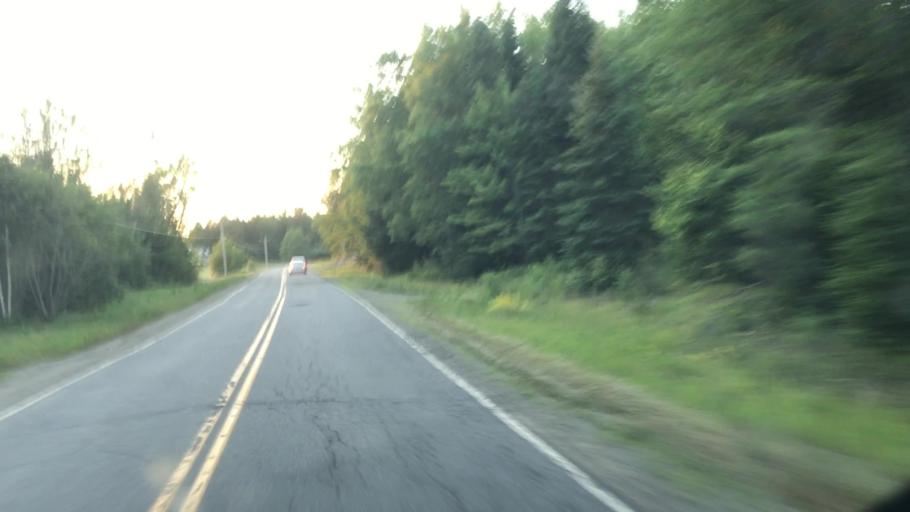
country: US
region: Maine
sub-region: Penobscot County
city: Medway
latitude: 45.6049
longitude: -68.2538
